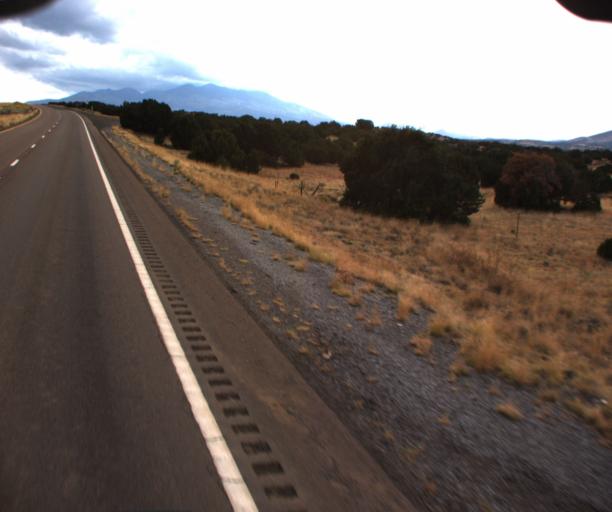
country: US
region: Arizona
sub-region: Coconino County
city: Flagstaff
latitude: 35.4947
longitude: -111.5540
